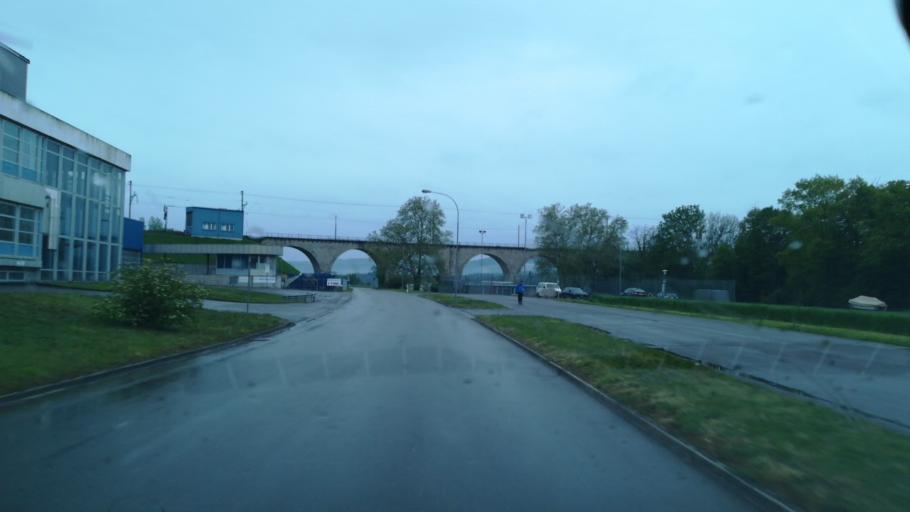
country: CH
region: Zurich
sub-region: Bezirk Buelach
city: Seglingen
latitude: 47.5754
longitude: 8.5120
